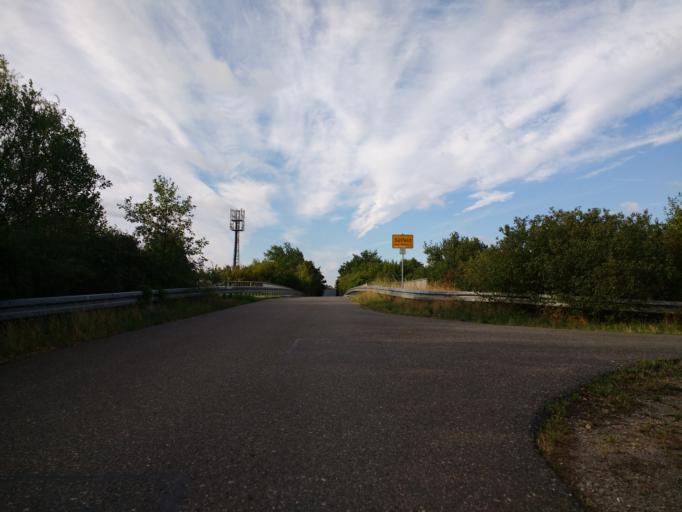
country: DE
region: Lower Saxony
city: Osloss
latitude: 52.4224
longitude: 10.6866
